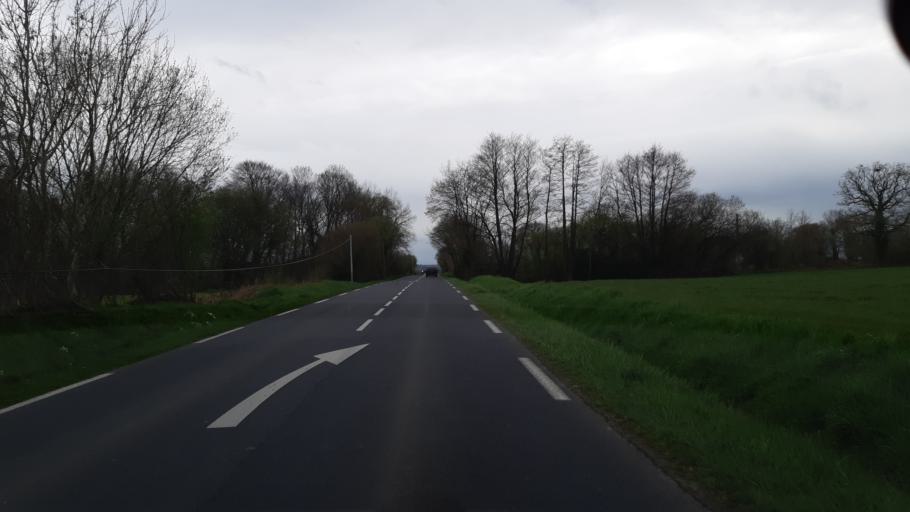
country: FR
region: Lower Normandy
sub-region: Departement de la Manche
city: Tessy-sur-Vire
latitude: 49.0176
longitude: -1.1479
